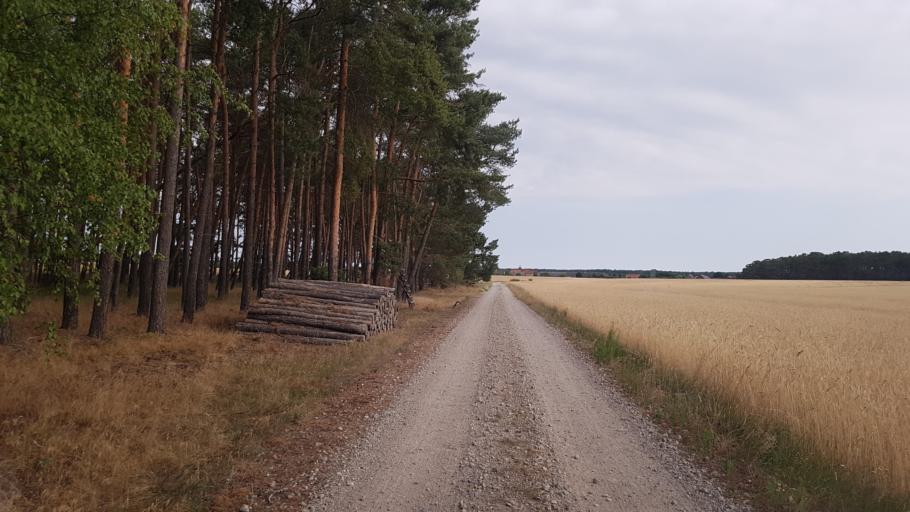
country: DE
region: Brandenburg
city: Linthe
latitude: 52.1052
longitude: 12.7886
